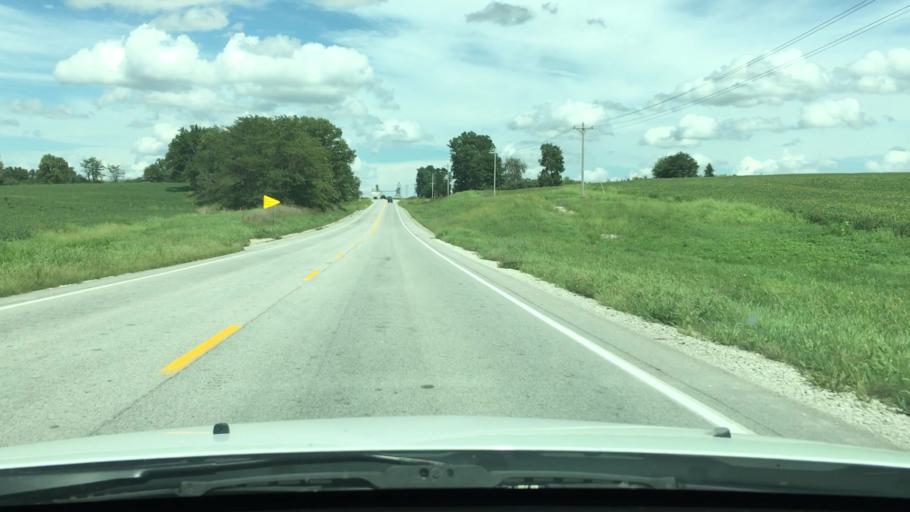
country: US
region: Illinois
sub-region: Pike County
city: Griggsville
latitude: 39.6657
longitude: -90.7717
